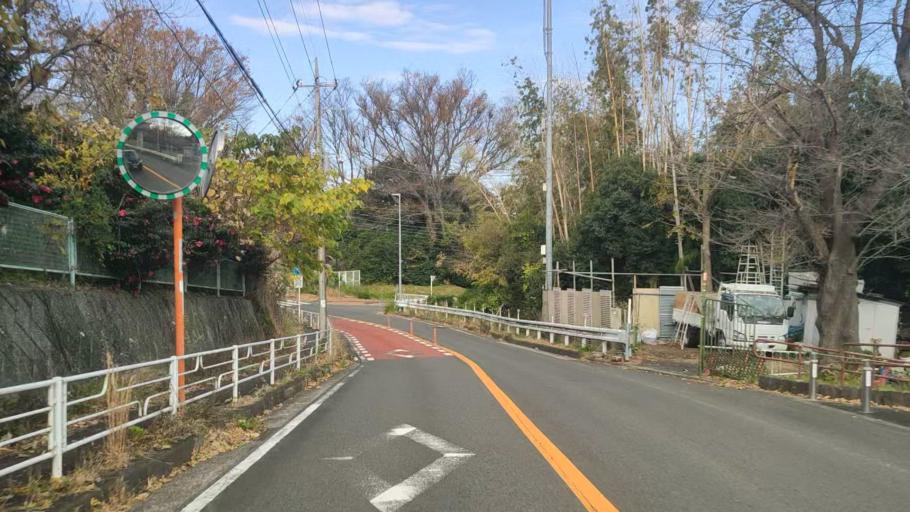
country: JP
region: Kanagawa
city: Minami-rinkan
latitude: 35.4532
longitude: 139.5393
